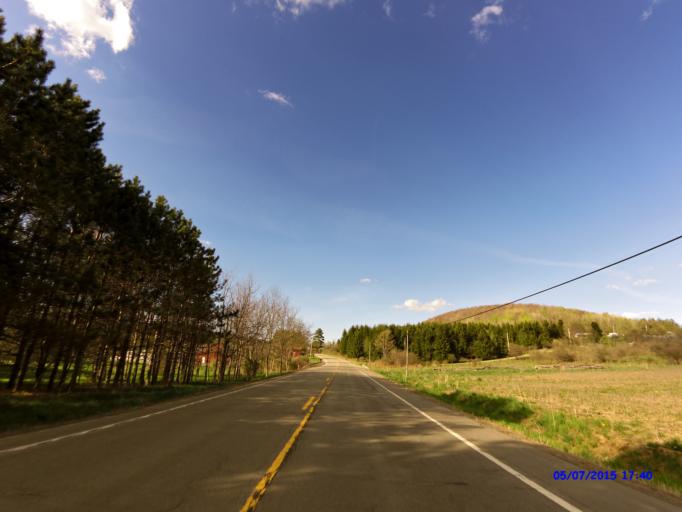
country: US
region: New York
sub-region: Cattaraugus County
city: Franklinville
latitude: 42.2753
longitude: -78.5362
